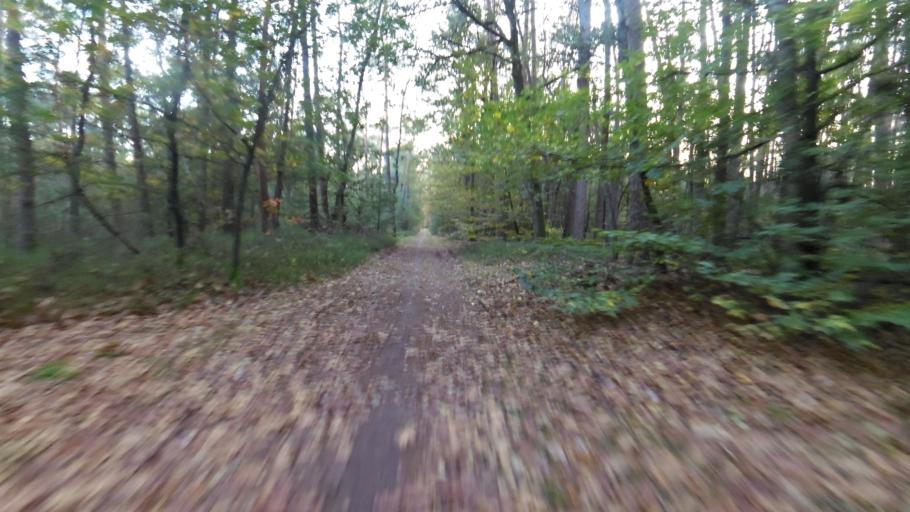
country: NL
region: Gelderland
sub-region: Gemeente Epe
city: Epe
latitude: 52.3677
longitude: 5.9704
